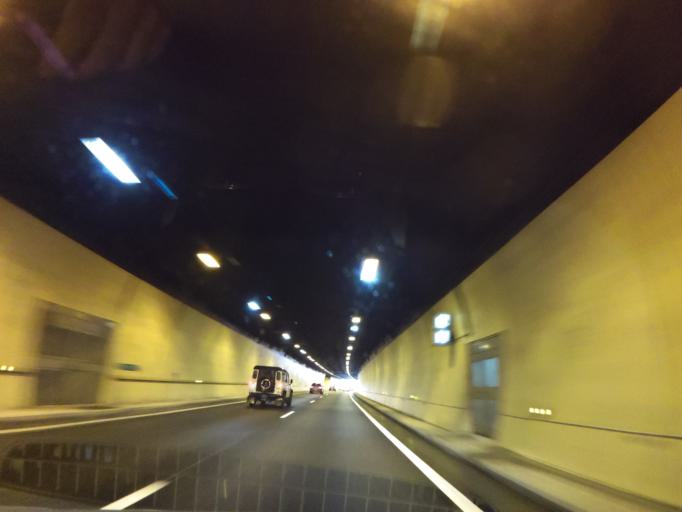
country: FR
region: Rhone-Alpes
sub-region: Departement de l'Ain
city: Saint-Martin-du-Frene
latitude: 46.1274
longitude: 5.5791
